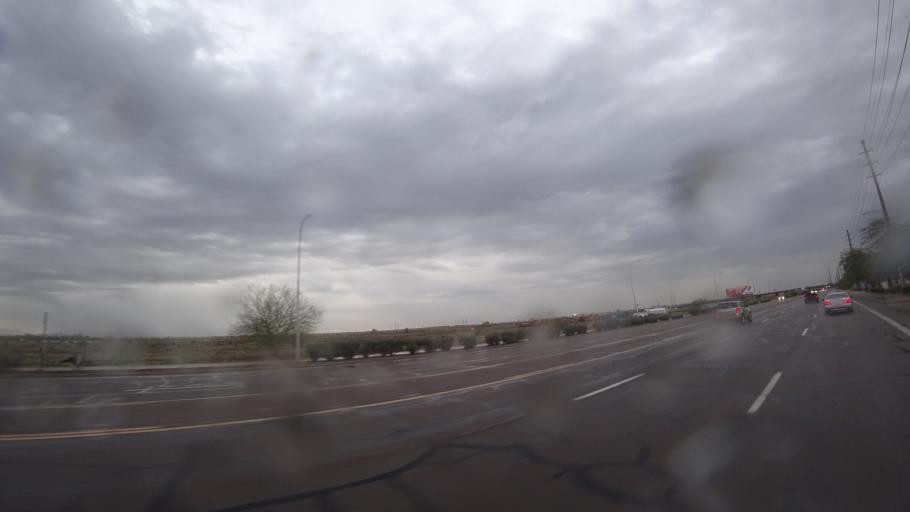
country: US
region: Arizona
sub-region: Maricopa County
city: Tempe
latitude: 33.4461
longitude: -111.9095
